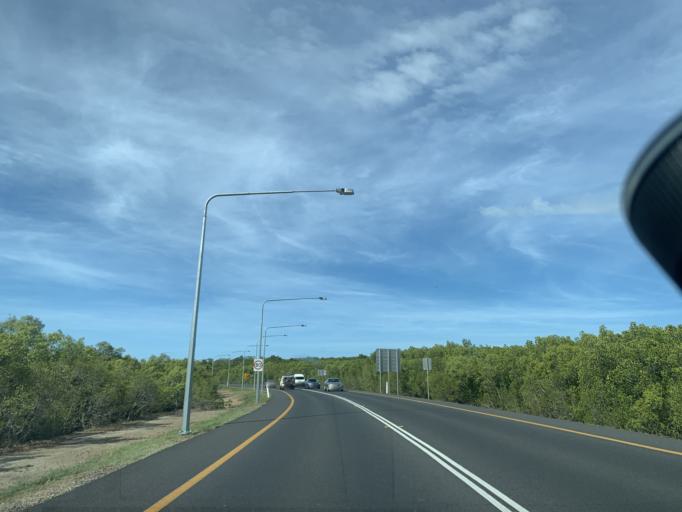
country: AU
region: Queensland
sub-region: Cairns
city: Cairns
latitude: -16.8956
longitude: 145.7592
